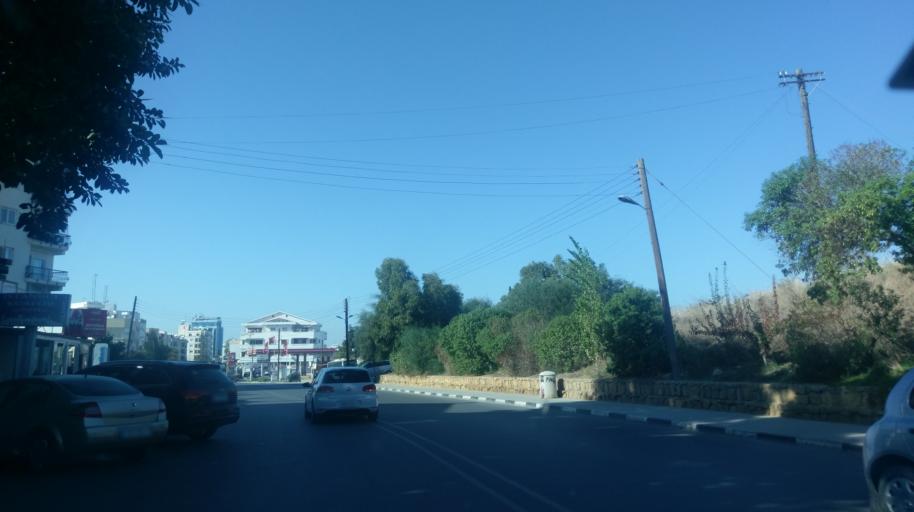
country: CY
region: Ammochostos
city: Famagusta
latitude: 35.1212
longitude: 33.9379
